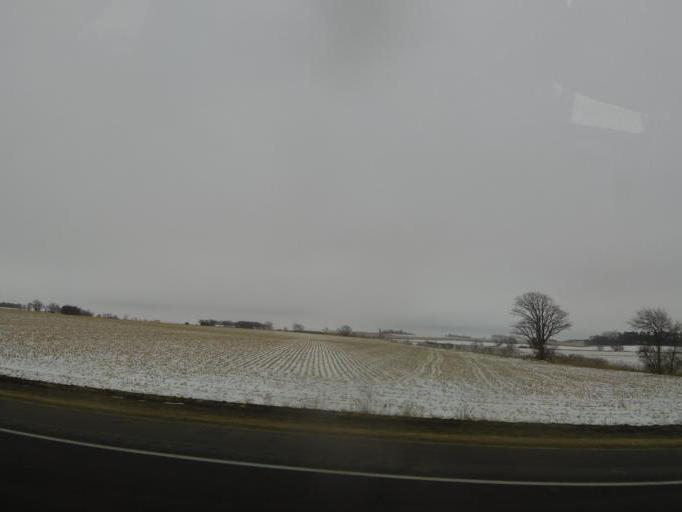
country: US
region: Iowa
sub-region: Chickasaw County
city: New Hampton
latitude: 43.2555
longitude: -92.2974
